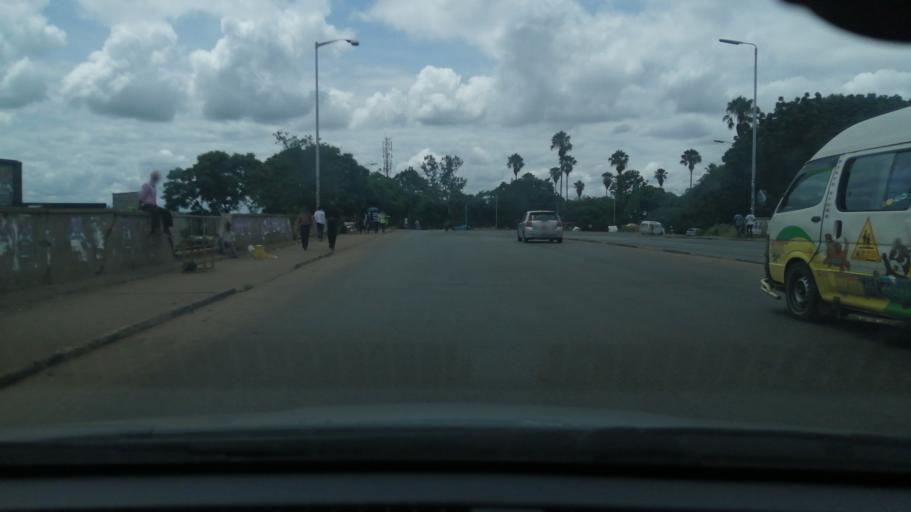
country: ZW
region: Harare
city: Harare
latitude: -17.8451
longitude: 31.0391
